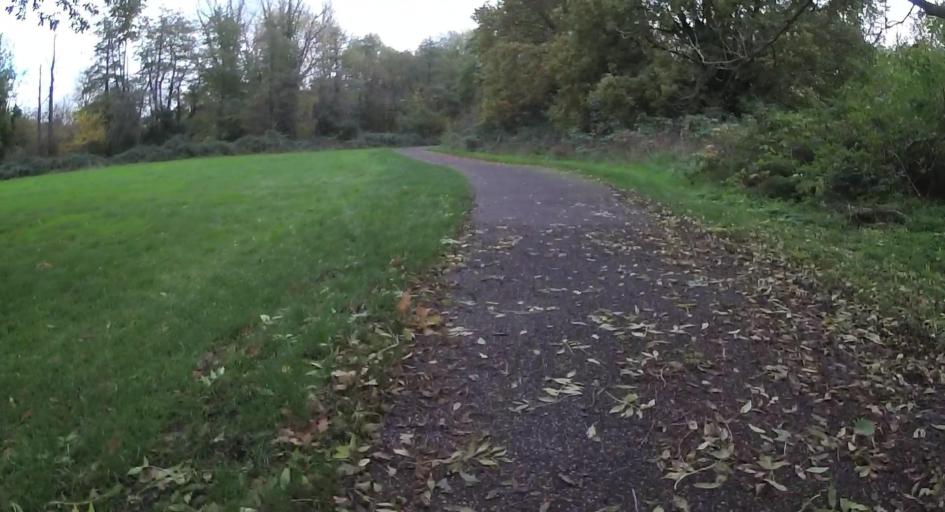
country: GB
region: England
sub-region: Wokingham
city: Wokingham
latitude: 51.4155
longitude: -0.8529
